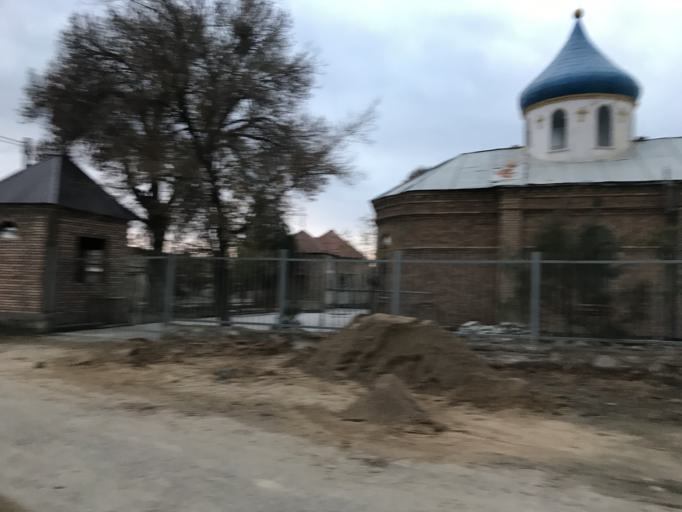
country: UZ
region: Bukhara
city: Kogon
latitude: 39.7216
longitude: 64.5601
